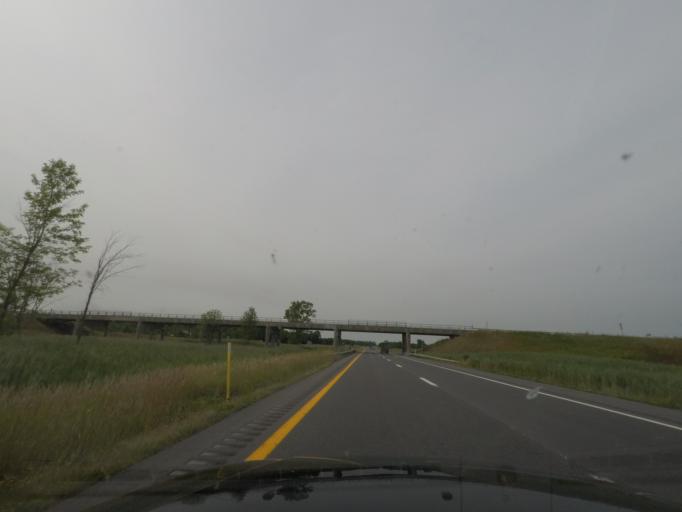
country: US
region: New York
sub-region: Clinton County
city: Cumberland Head
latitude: 44.7802
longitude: -73.4369
